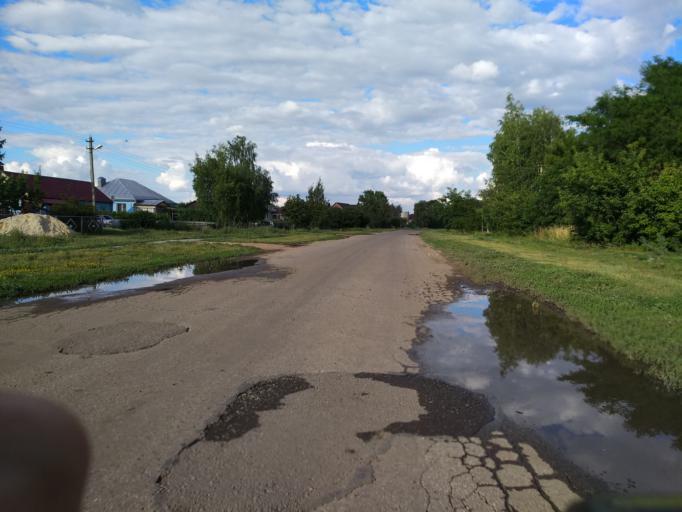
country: RU
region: Lipetsk
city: Dobrinka
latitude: 52.0380
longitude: 40.5321
